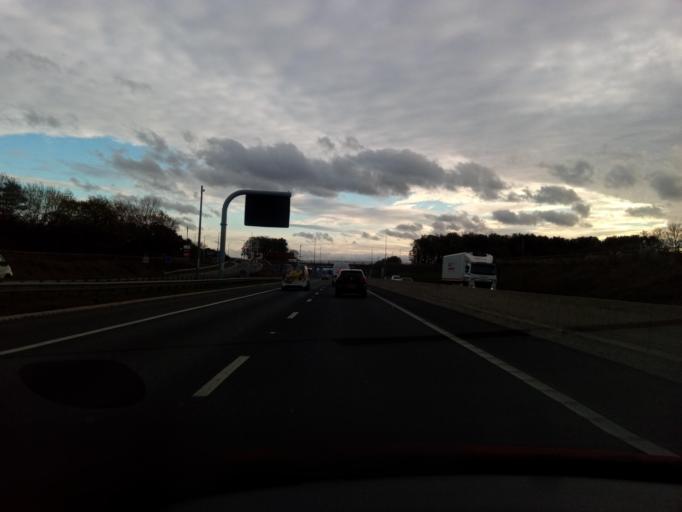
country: GB
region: England
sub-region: North Yorkshire
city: Catterick
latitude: 54.4450
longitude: -1.6684
